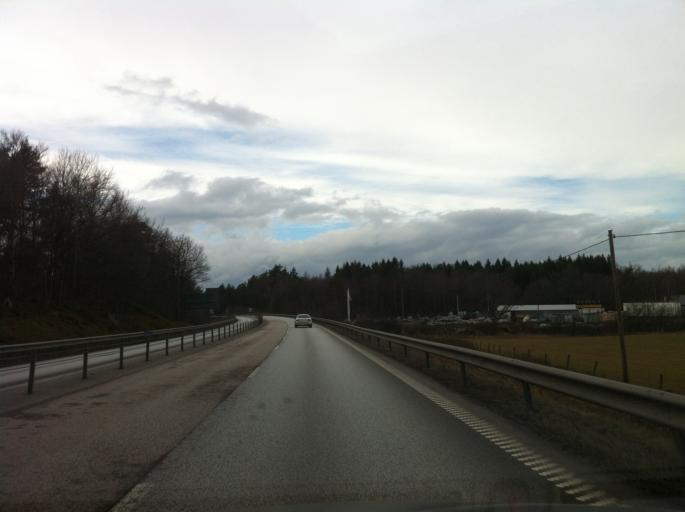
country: SE
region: Blekinge
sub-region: Karlshamns Kommun
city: Karlshamn
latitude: 56.1958
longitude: 14.9703
